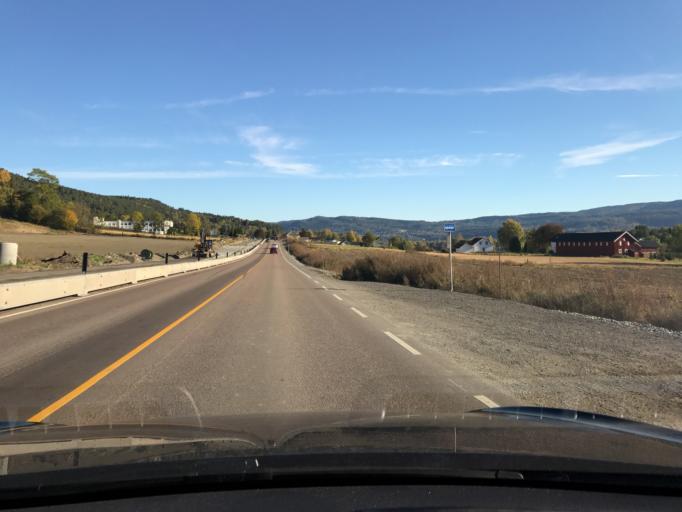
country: NO
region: Buskerud
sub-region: Ovre Eiker
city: Hokksund
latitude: 59.7717
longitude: 9.9487
